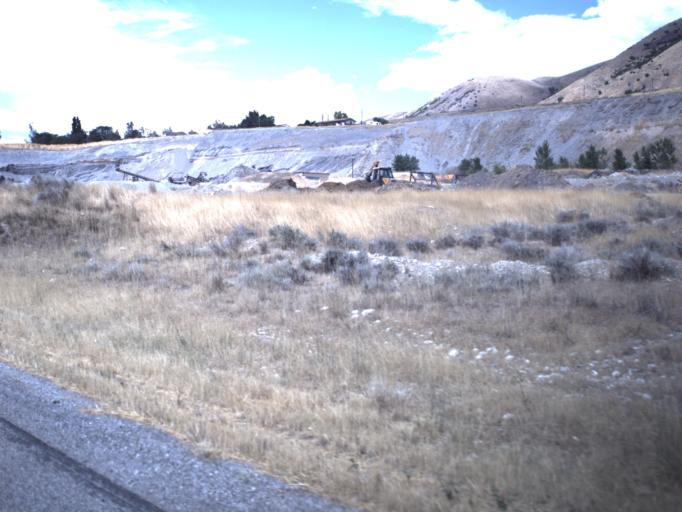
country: US
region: Utah
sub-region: Box Elder County
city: Elwood
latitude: 41.7310
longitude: -112.0982
